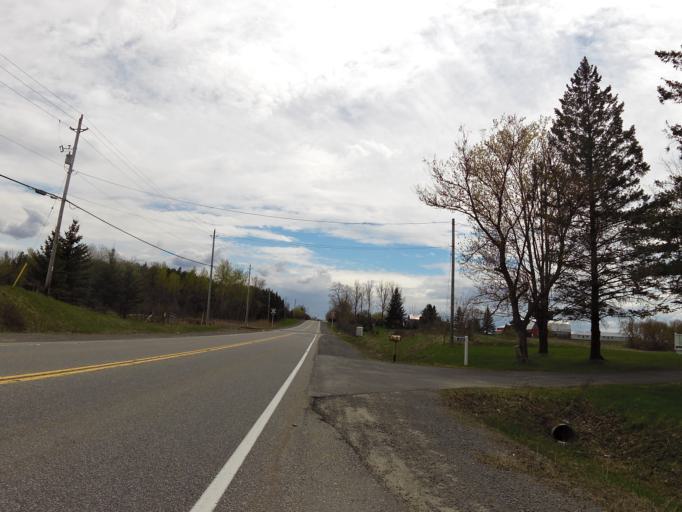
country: CA
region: Ontario
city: Hawkesbury
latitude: 45.5453
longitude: -74.6388
